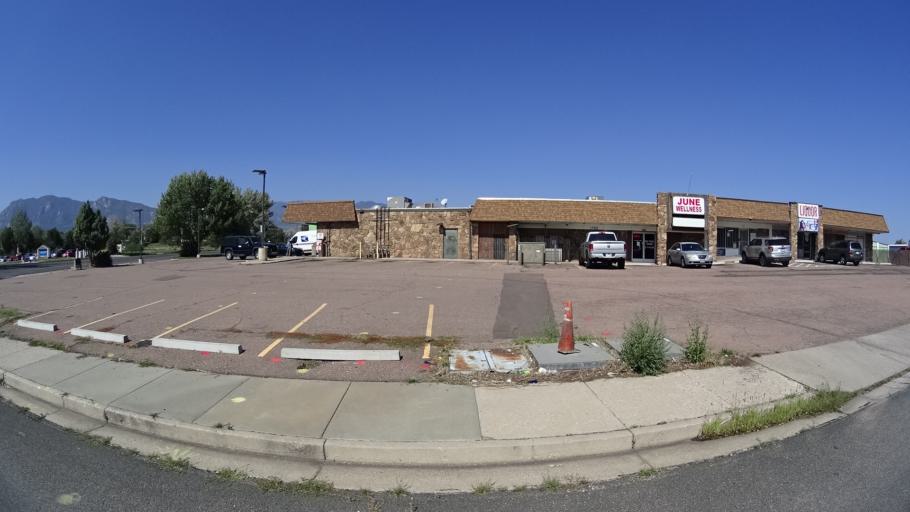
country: US
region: Colorado
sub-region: El Paso County
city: Stratmoor
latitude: 38.8063
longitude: -104.7778
